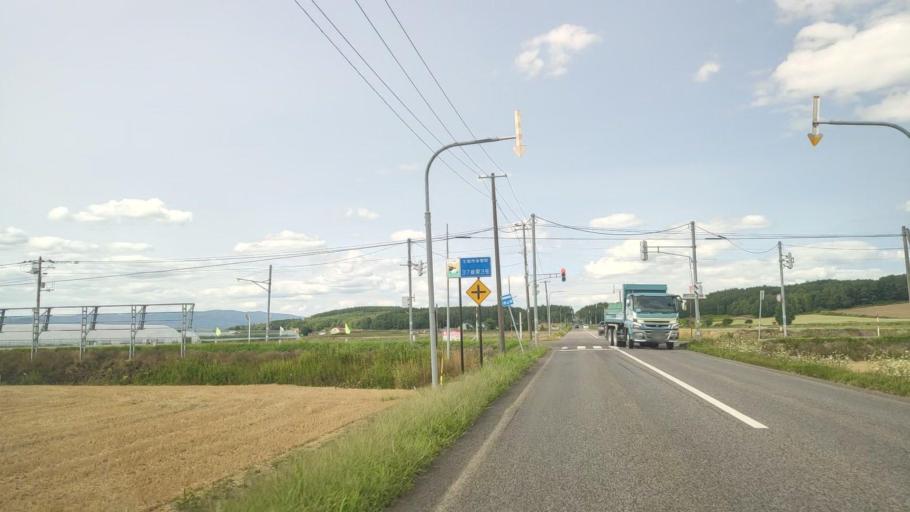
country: JP
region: Hokkaido
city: Nayoro
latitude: 44.2356
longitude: 142.4157
